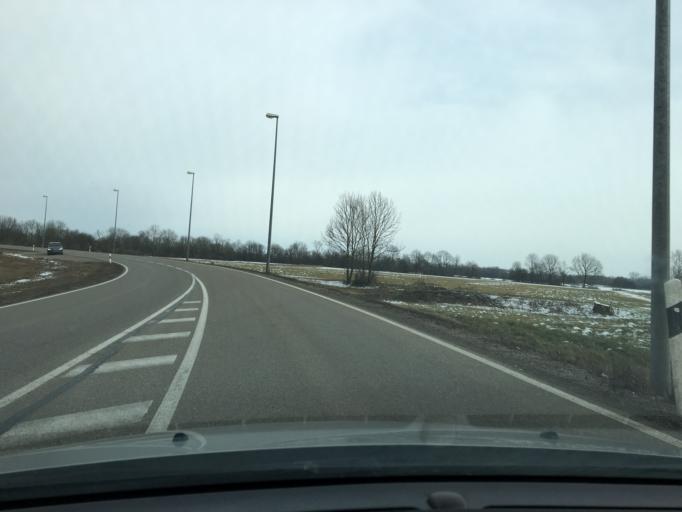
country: DE
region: Bavaria
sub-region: Upper Bavaria
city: Oberding
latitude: 48.3499
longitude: 11.8063
